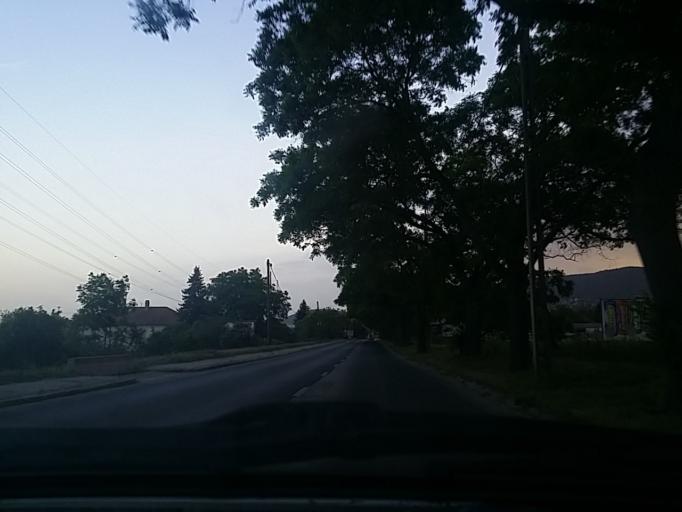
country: HU
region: Pest
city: Urom
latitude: 47.5740
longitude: 19.0307
